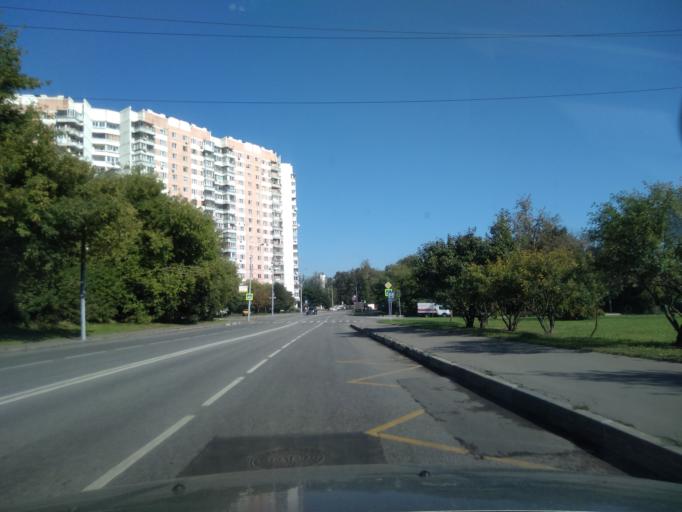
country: RU
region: Moscow
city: Strogino
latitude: 55.8361
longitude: 37.4056
